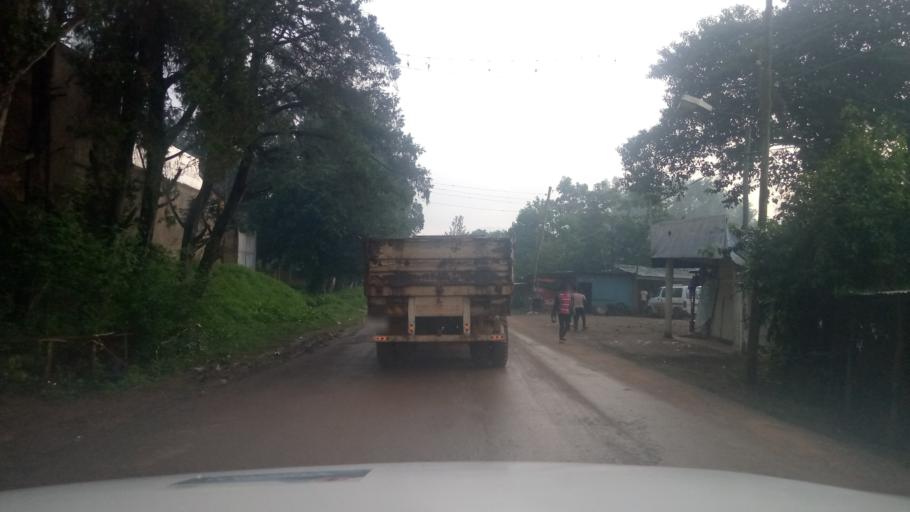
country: ET
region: Oromiya
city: Jima
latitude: 7.6774
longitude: 36.8344
